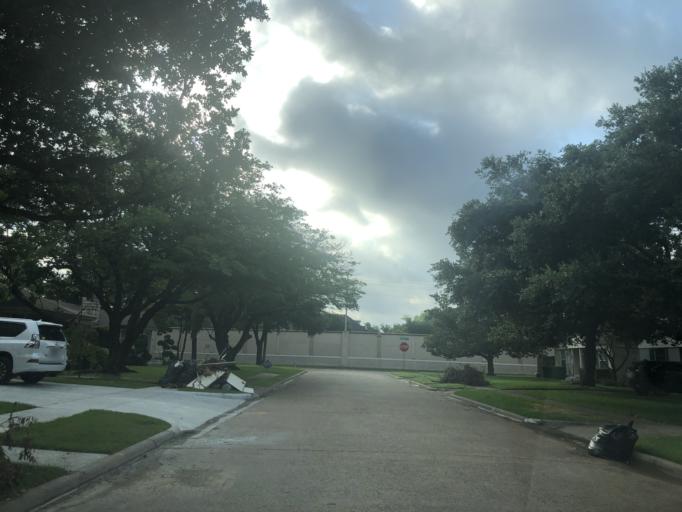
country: US
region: Texas
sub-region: Dallas County
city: University Park
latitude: 32.8552
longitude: -96.8138
